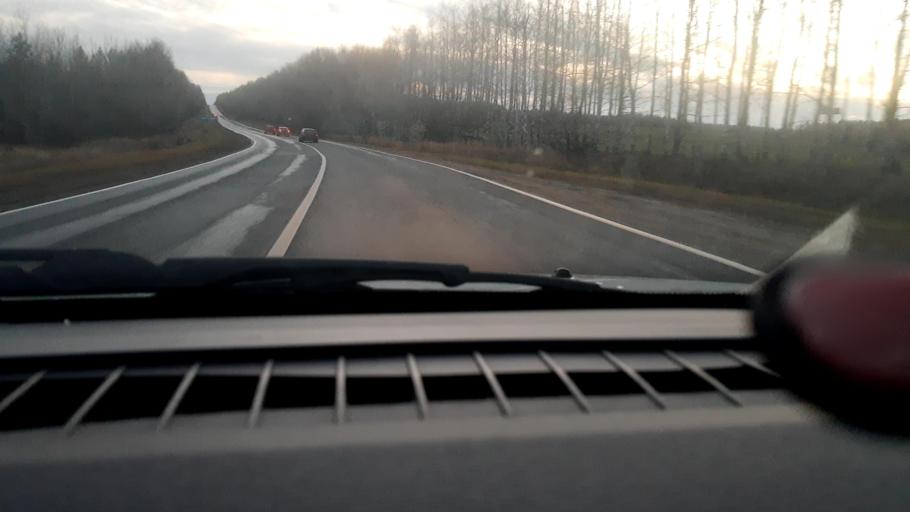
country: RU
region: Nizjnij Novgorod
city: Vladimirskoye
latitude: 56.9567
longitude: 45.0952
